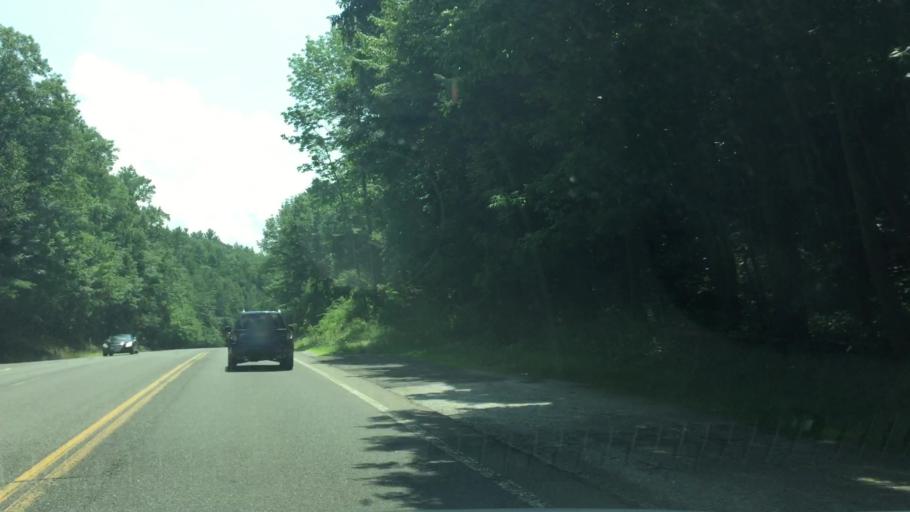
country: US
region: Massachusetts
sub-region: Berkshire County
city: Housatonic
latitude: 42.2387
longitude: -73.3349
